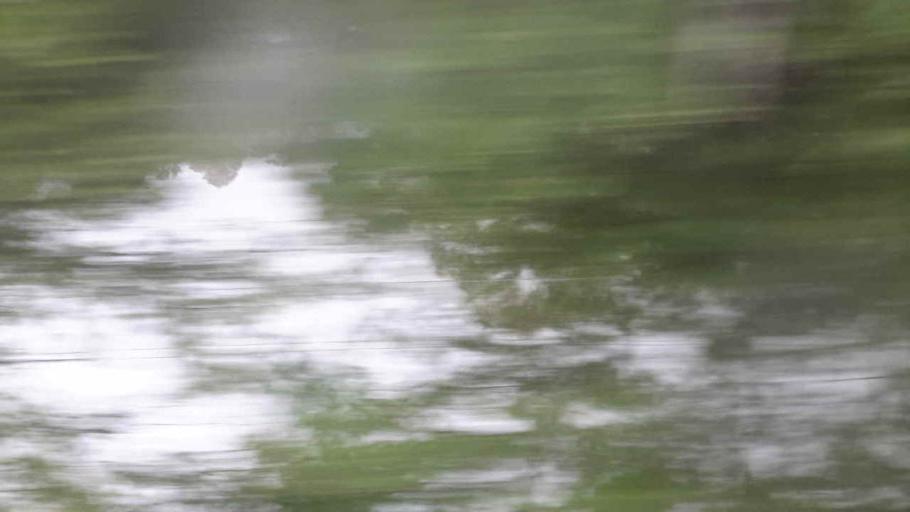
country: AU
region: New South Wales
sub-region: Camden
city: Camden South
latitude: -34.0742
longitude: 150.6962
